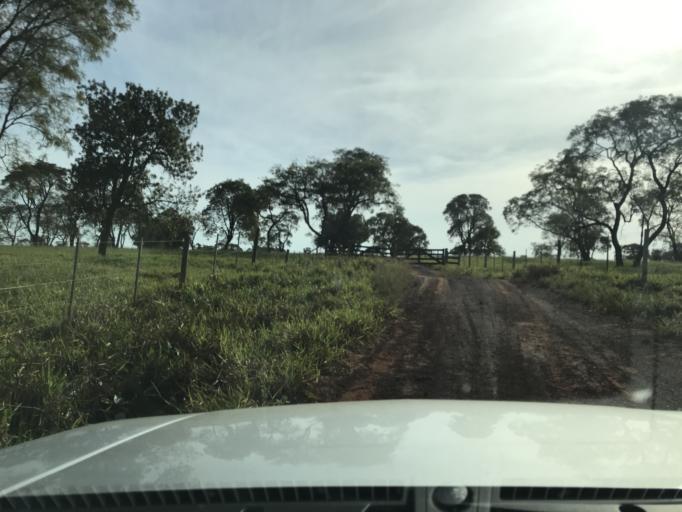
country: BR
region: Mato Grosso do Sul
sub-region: Iguatemi
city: Iguatemi
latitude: -23.6444
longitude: -54.5743
